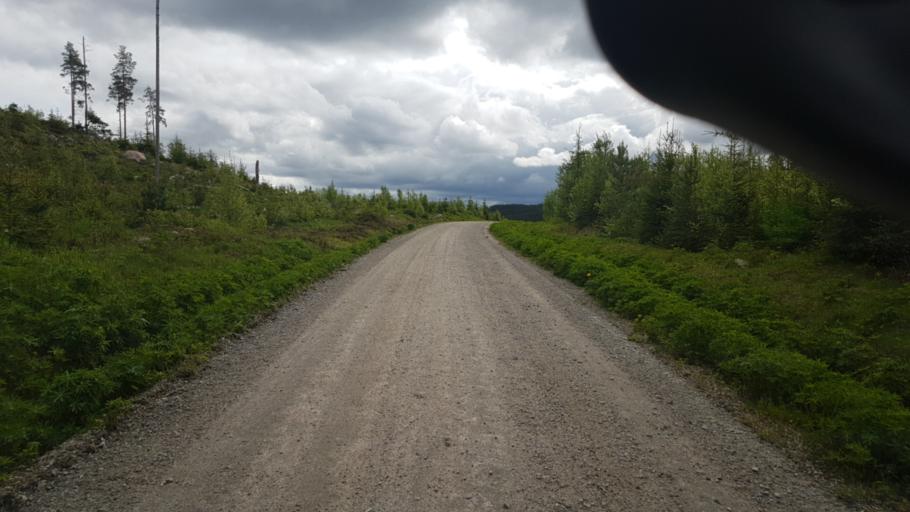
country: SE
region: Vaermland
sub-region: Arvika Kommun
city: Arvika
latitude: 59.8306
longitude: 12.8271
